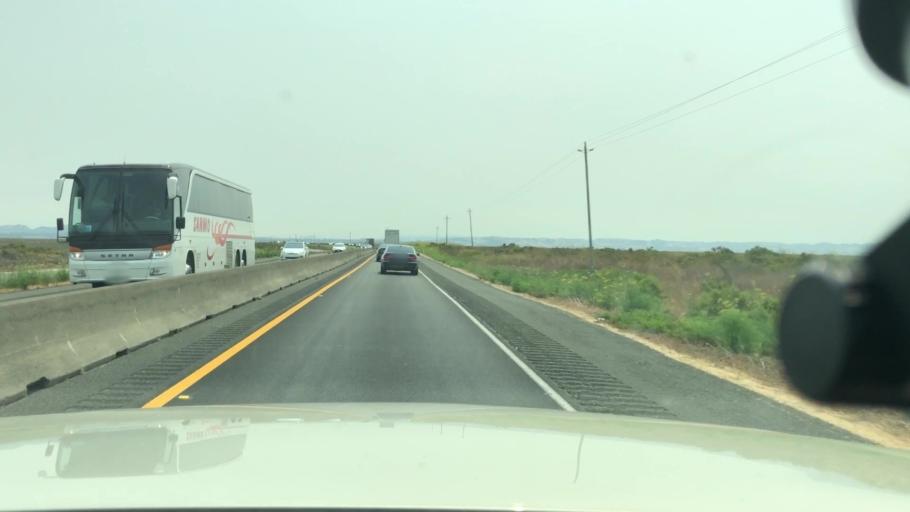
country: US
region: California
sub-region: Napa County
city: American Canyon
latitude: 38.1474
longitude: -122.3783
